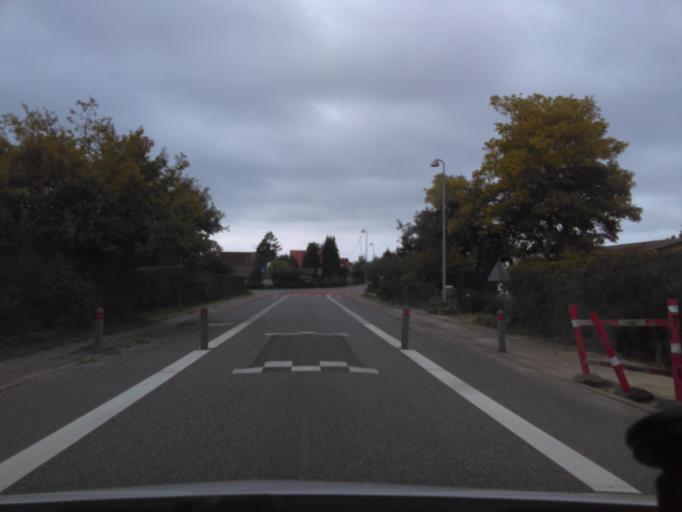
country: DK
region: Capital Region
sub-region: Fureso Kommune
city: Farum
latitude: 55.8108
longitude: 12.3458
